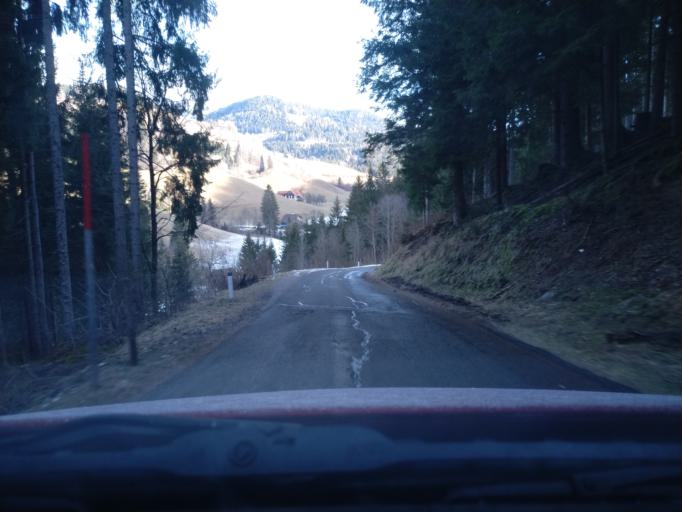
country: AT
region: Carinthia
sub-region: Politischer Bezirk Villach Land
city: Arriach
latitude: 46.7249
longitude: 13.8797
